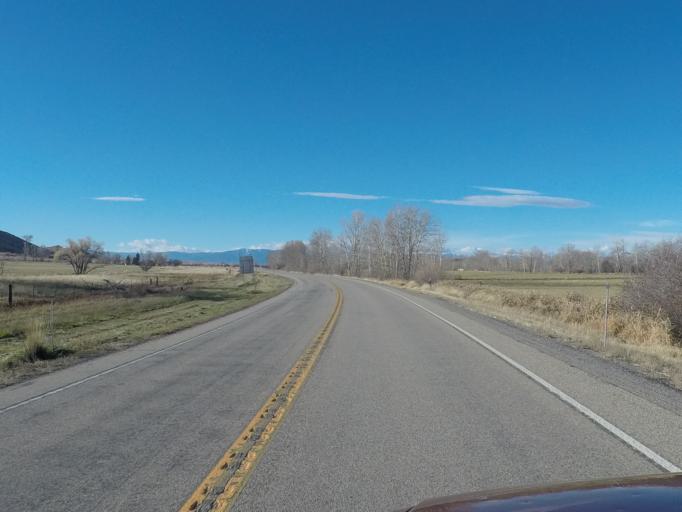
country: US
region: Montana
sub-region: Stillwater County
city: Columbus
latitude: 45.4545
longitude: -109.0739
